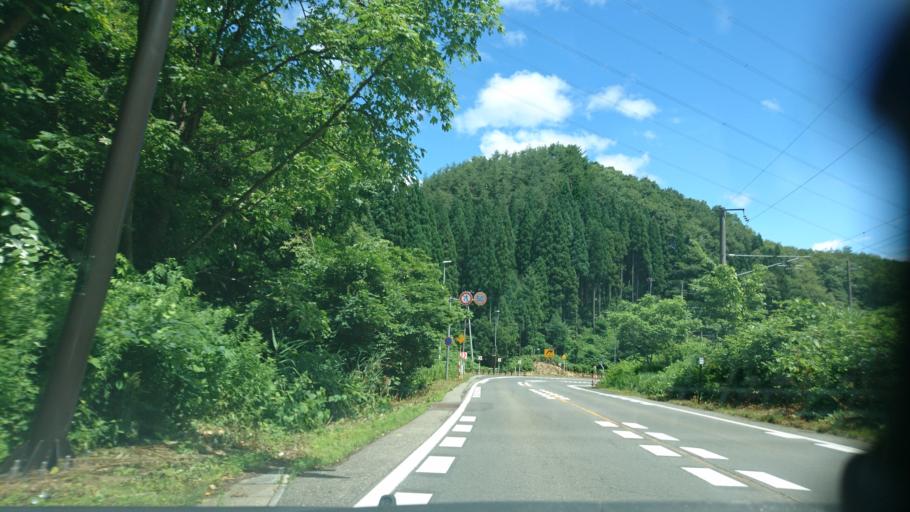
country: JP
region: Akita
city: Kakunodatemachi
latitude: 39.6772
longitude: 140.7000
